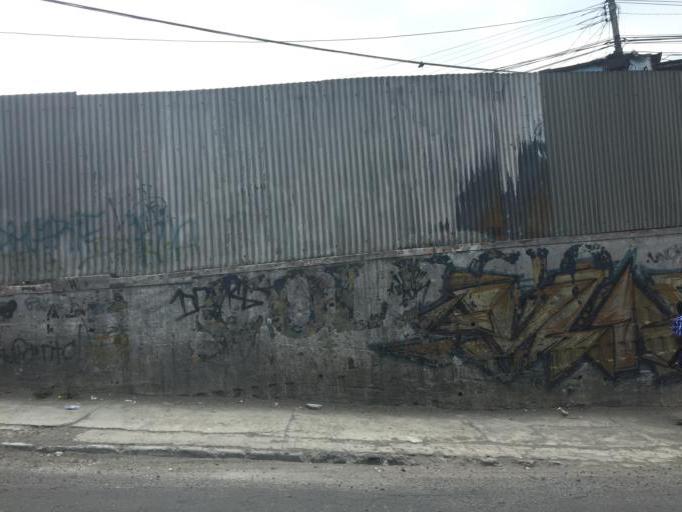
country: GT
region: Guatemala
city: Petapa
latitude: 14.5288
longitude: -90.5548
